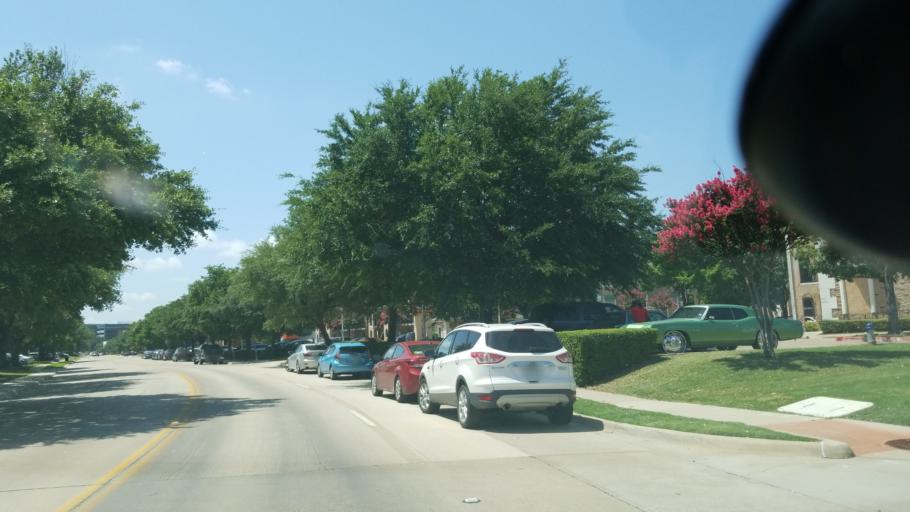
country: US
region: Texas
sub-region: Dallas County
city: University Park
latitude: 32.8257
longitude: -96.8691
